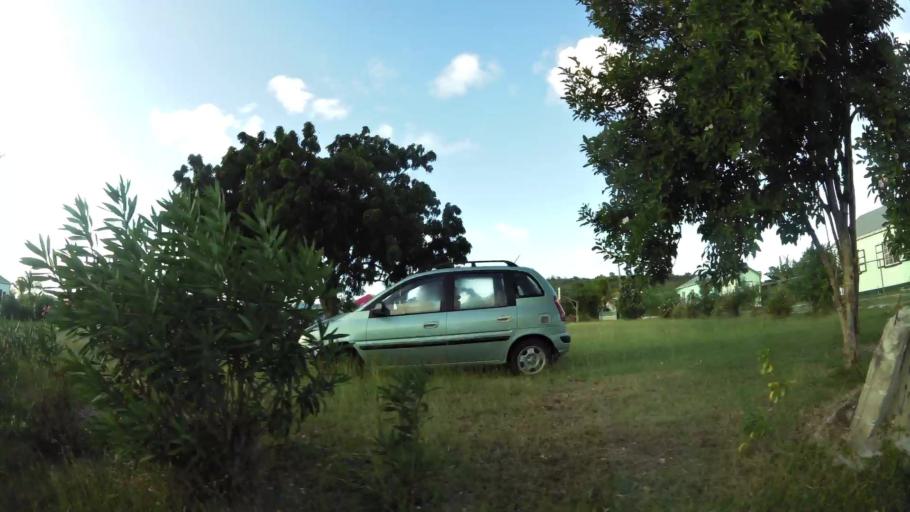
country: AG
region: Saint George
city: Piggotts
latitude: 17.1128
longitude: -61.7925
